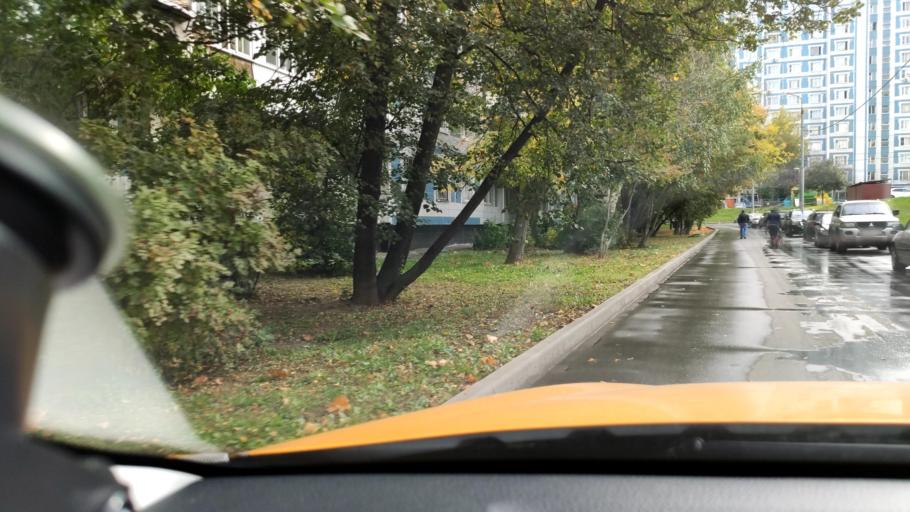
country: RU
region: Moskovskaya
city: Razvilka
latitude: 55.6072
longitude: 37.7496
